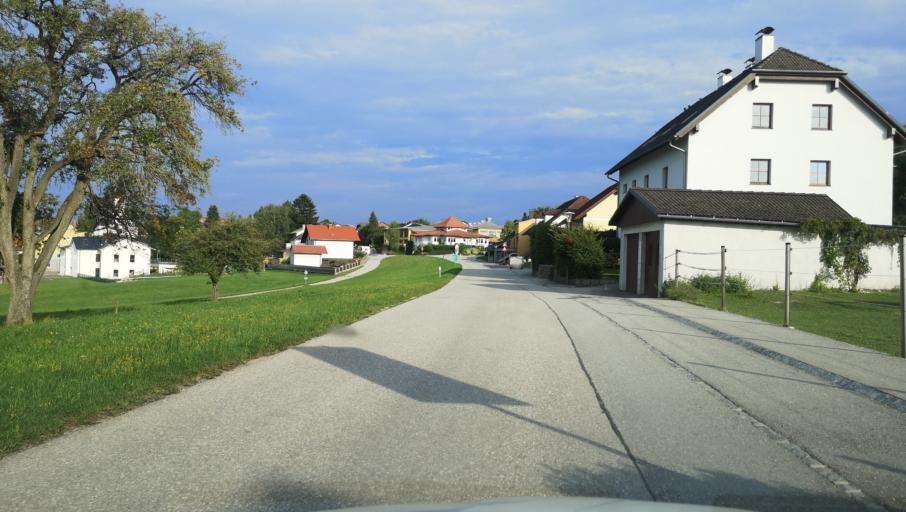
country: AT
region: Lower Austria
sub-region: Politischer Bezirk Amstetten
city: Amstetten
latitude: 48.1505
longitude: 14.8879
